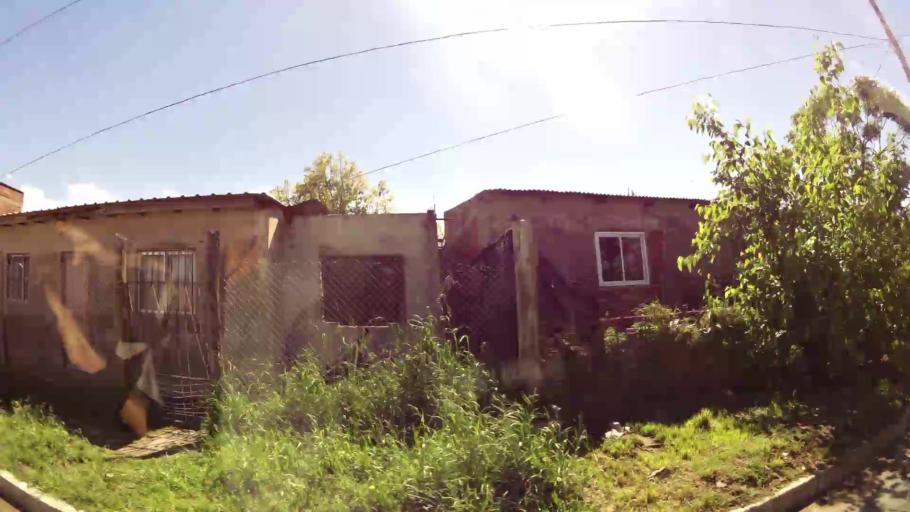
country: AR
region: Buenos Aires
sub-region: Partido de Quilmes
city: Quilmes
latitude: -34.6867
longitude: -58.3034
